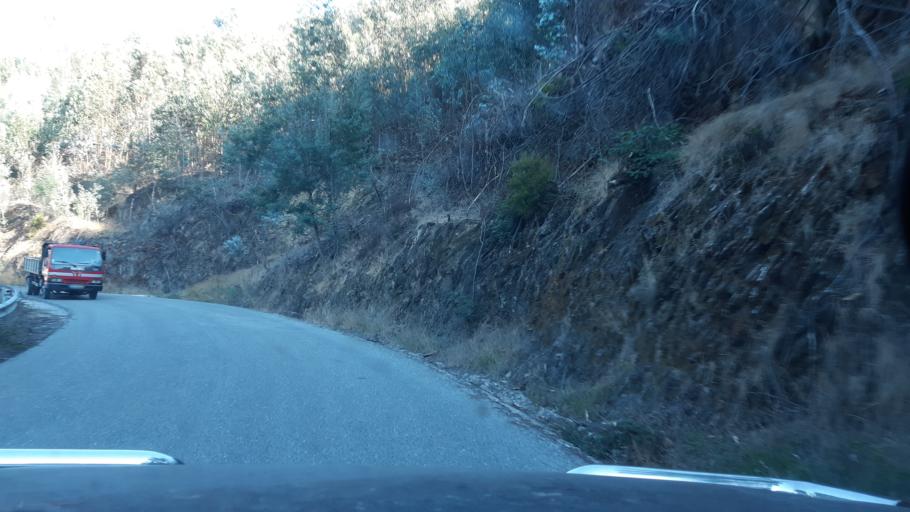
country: PT
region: Aveiro
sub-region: Agueda
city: Aguada de Cima
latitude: 40.5673
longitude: -8.3572
